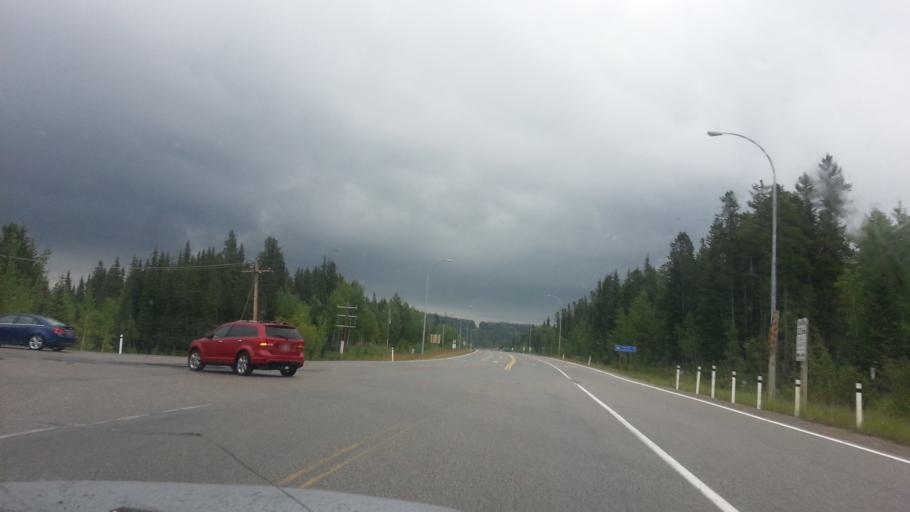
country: CA
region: Alberta
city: Cochrane
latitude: 50.9214
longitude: -114.5607
